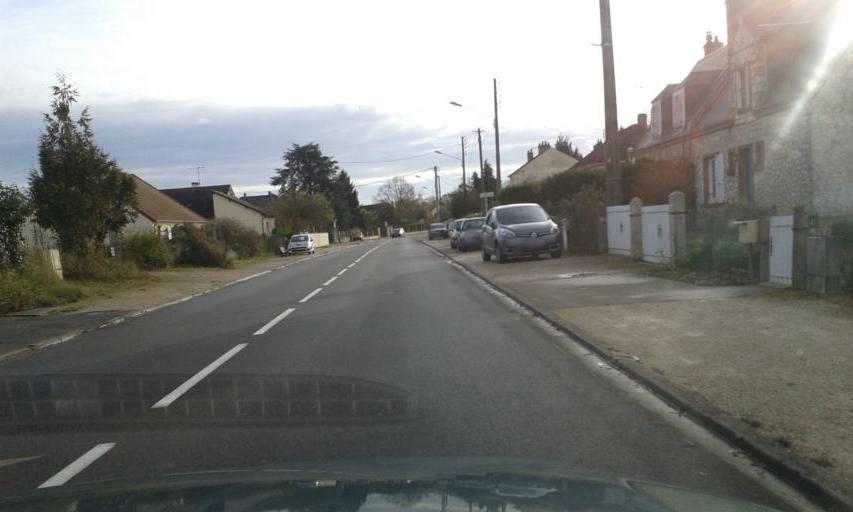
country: FR
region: Centre
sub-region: Departement du Loiret
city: Beaugency
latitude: 47.7862
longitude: 1.6286
